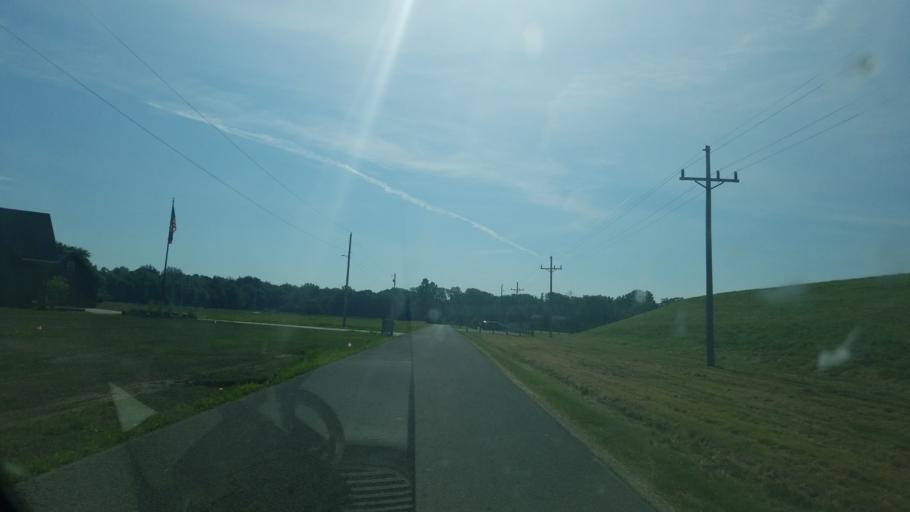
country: US
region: Ohio
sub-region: Hancock County
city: Findlay
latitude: 41.0275
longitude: -83.5624
